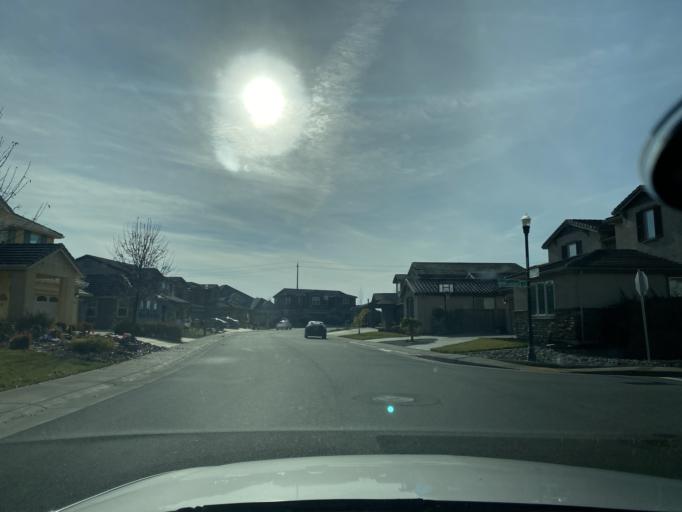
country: US
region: California
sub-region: Sacramento County
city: Elk Grove
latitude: 38.3960
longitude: -121.3834
